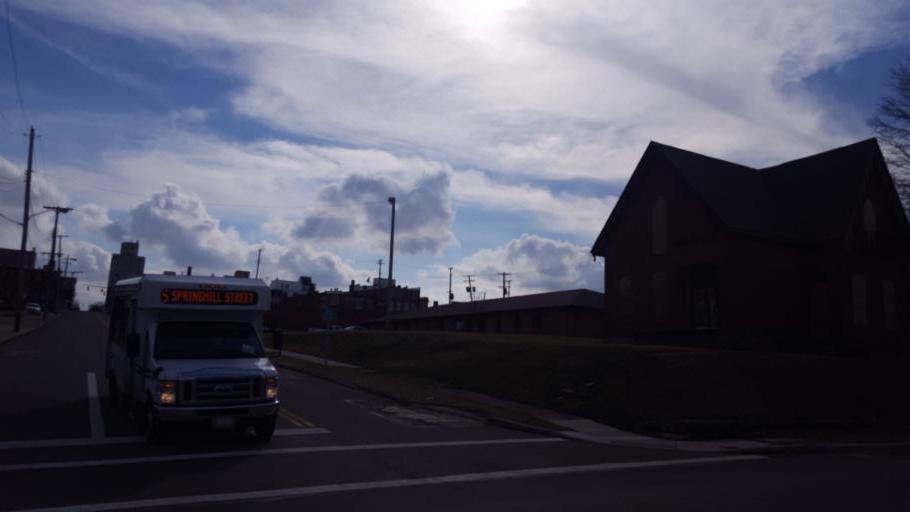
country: US
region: Ohio
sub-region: Richland County
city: Mansfield
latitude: 40.7631
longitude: -82.5162
